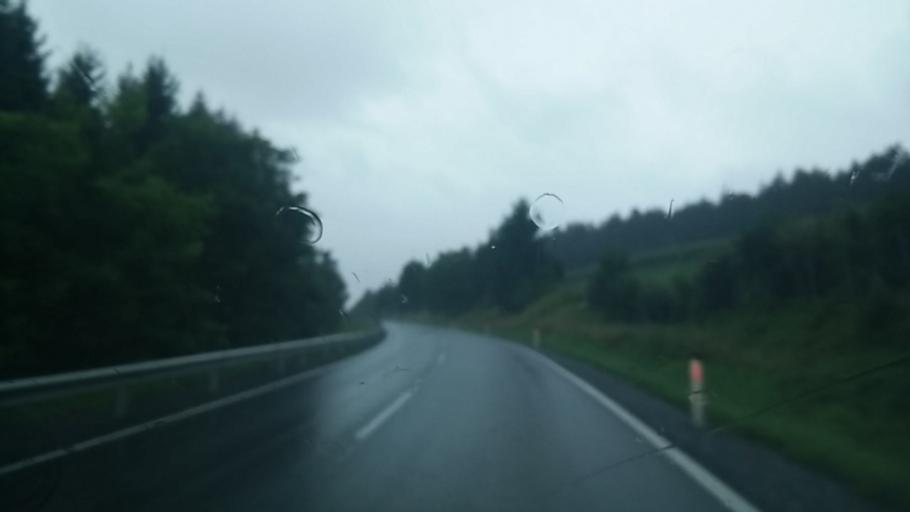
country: AT
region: Carinthia
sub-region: Politischer Bezirk Villach Land
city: Wernberg
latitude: 46.6131
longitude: 13.9740
